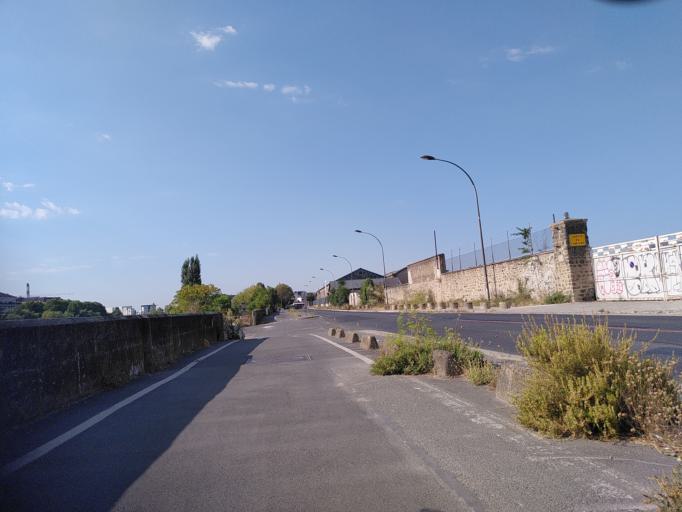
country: FR
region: Ile-de-France
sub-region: Departement du Val-de-Marne
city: Charenton-le-Pont
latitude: 48.8124
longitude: 2.4088
